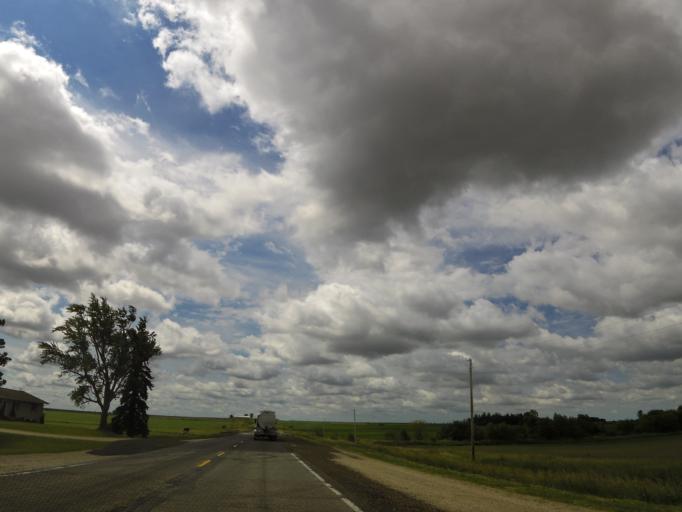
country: US
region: Iowa
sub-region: Howard County
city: Cresco
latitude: 43.3365
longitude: -92.2987
